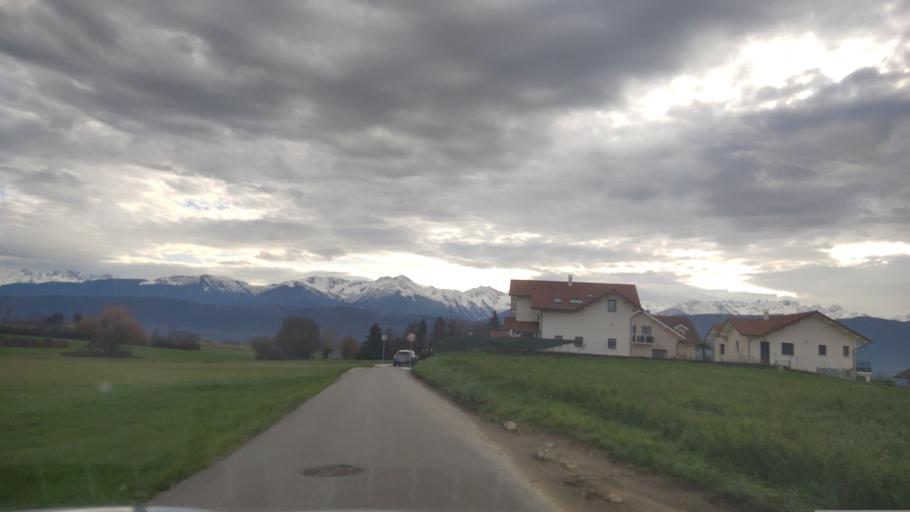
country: FR
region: Rhone-Alpes
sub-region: Departement de la Savoie
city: Les Marches
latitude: 45.5031
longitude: 6.0036
